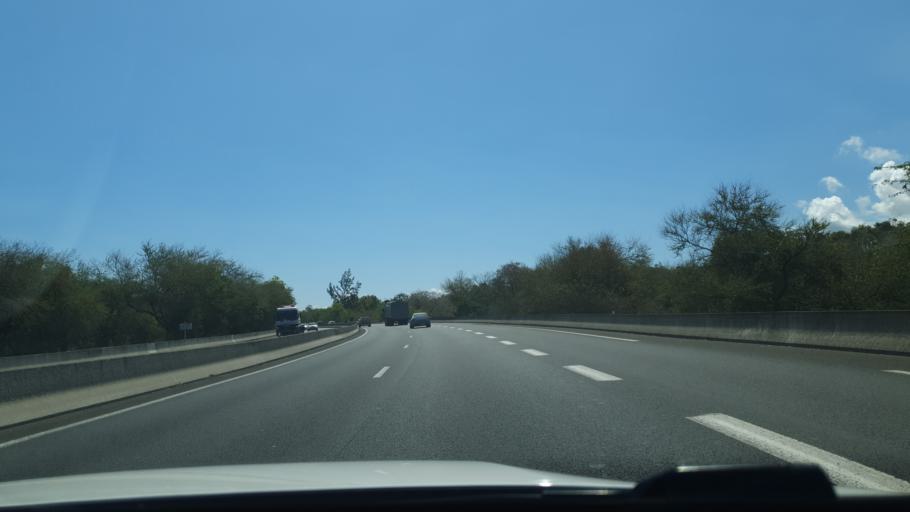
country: RE
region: Reunion
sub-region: Reunion
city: Les Avirons
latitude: -21.2795
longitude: 55.3643
